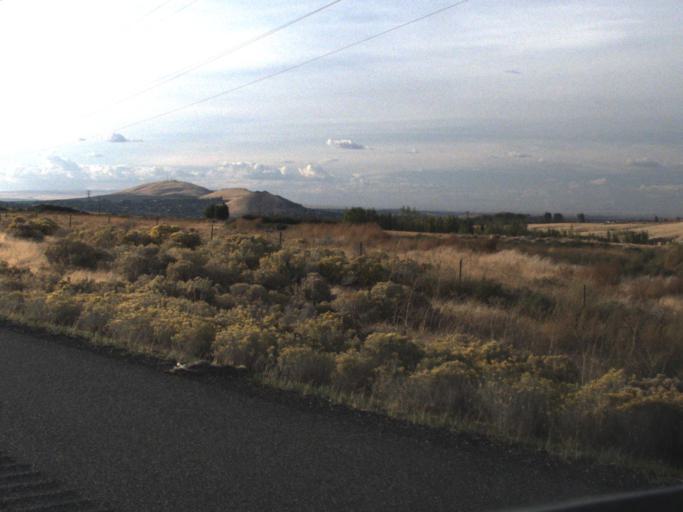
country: US
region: Washington
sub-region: Franklin County
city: West Pasco
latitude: 46.1746
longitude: -119.2180
